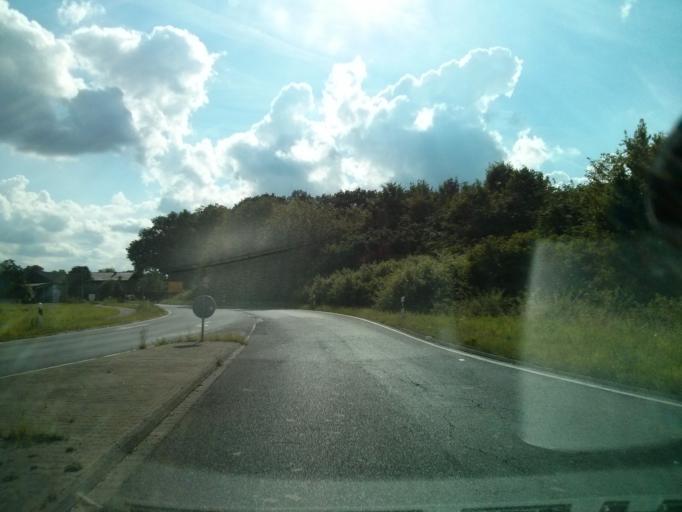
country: DE
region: North Rhine-Westphalia
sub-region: Regierungsbezirk Dusseldorf
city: Willich
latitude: 51.2930
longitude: 6.5261
